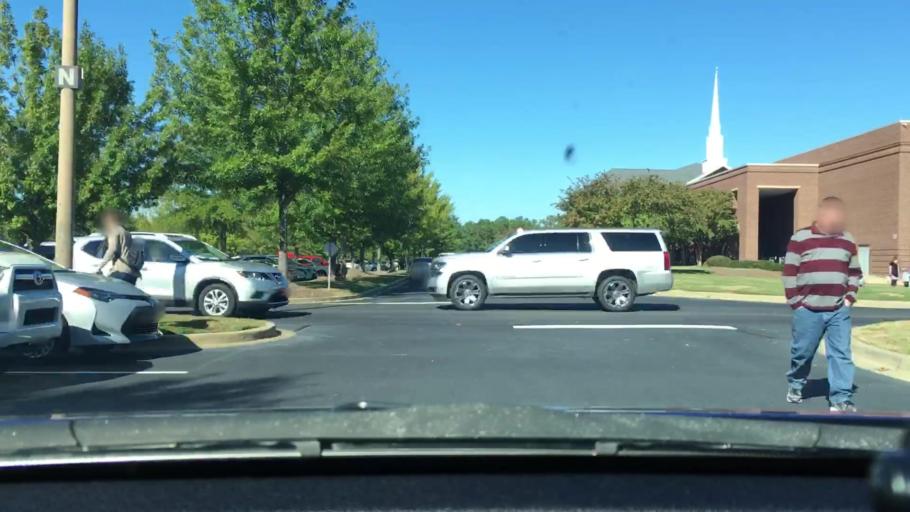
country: US
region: South Carolina
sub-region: Lexington County
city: Irmo
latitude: 34.0846
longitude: -81.1513
